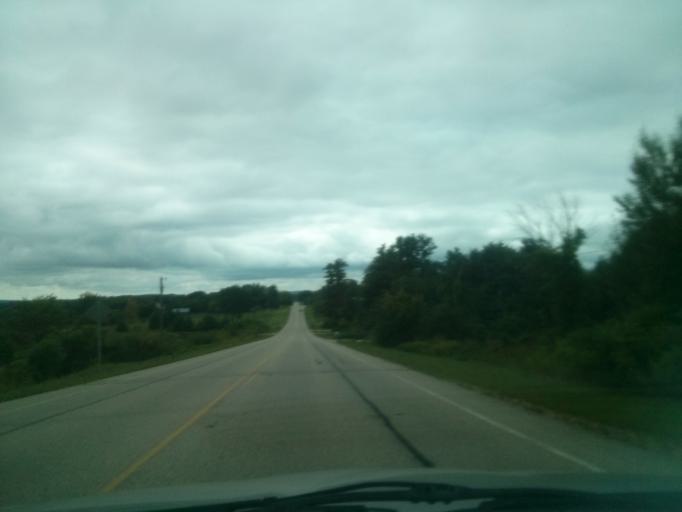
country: US
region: Wisconsin
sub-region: Pierce County
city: Spring Valley
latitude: 44.8322
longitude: -92.3413
